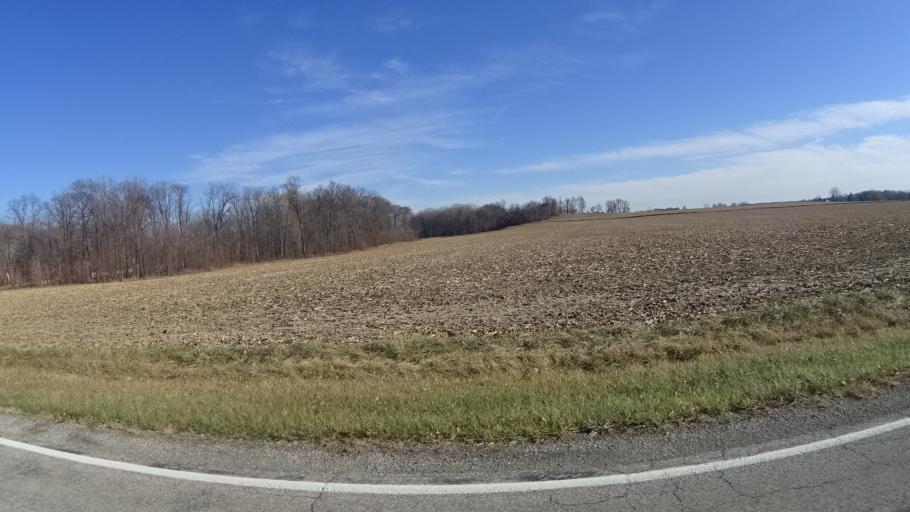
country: US
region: Ohio
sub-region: Lorain County
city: South Amherst
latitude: 41.3440
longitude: -82.3320
